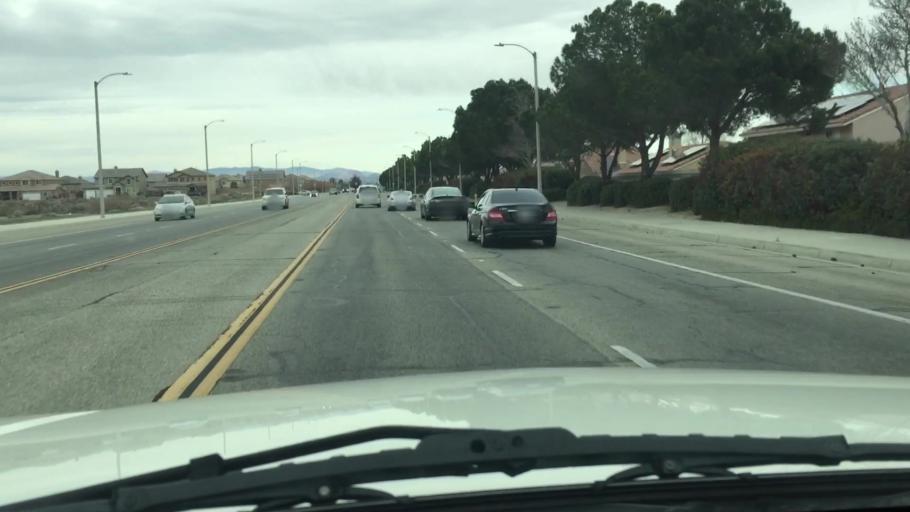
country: US
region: California
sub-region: Los Angeles County
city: Lancaster
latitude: 34.6909
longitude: -118.1838
